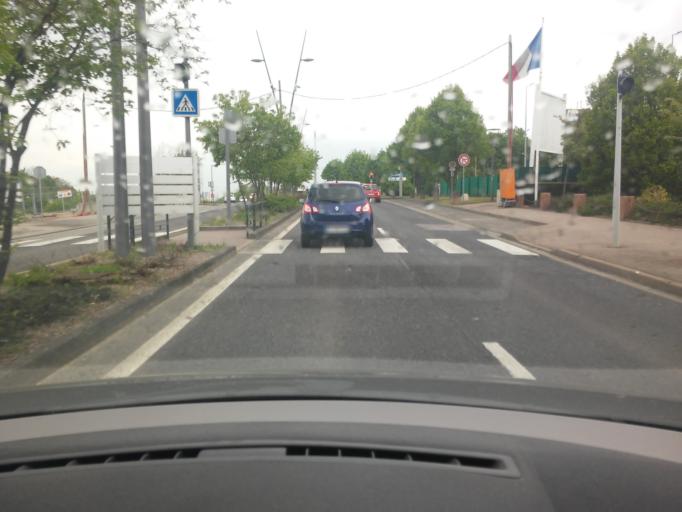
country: FR
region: Lorraine
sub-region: Departement de Meurthe-et-Moselle
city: Laxou
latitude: 48.6950
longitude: 6.1257
